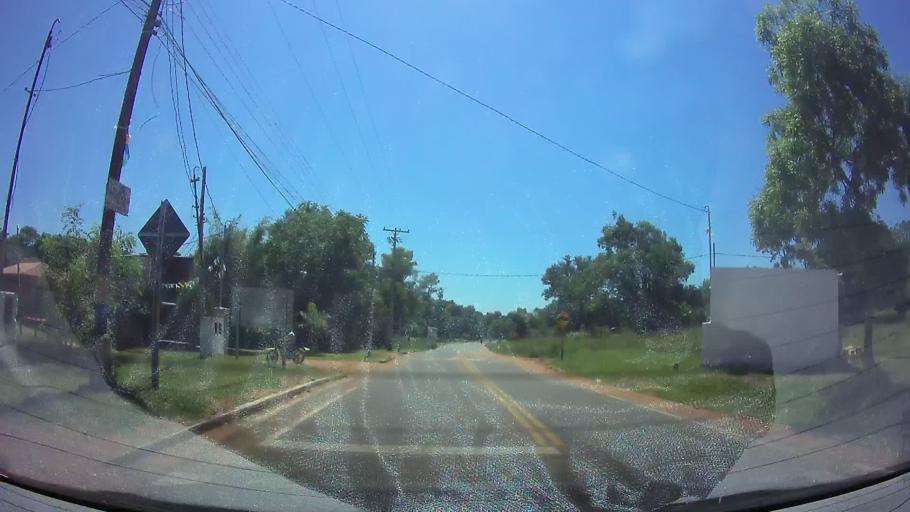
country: PY
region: Central
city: Aregua
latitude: -25.2592
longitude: -57.4474
